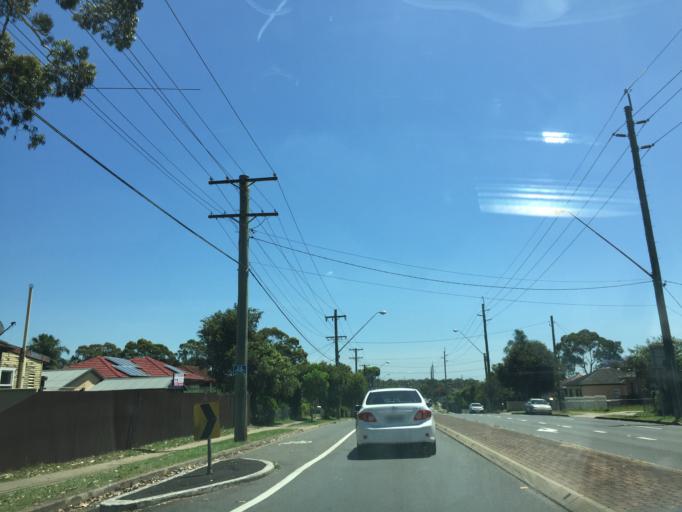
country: AU
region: New South Wales
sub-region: Parramatta
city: Constitution Hill
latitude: -33.7864
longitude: 150.9656
